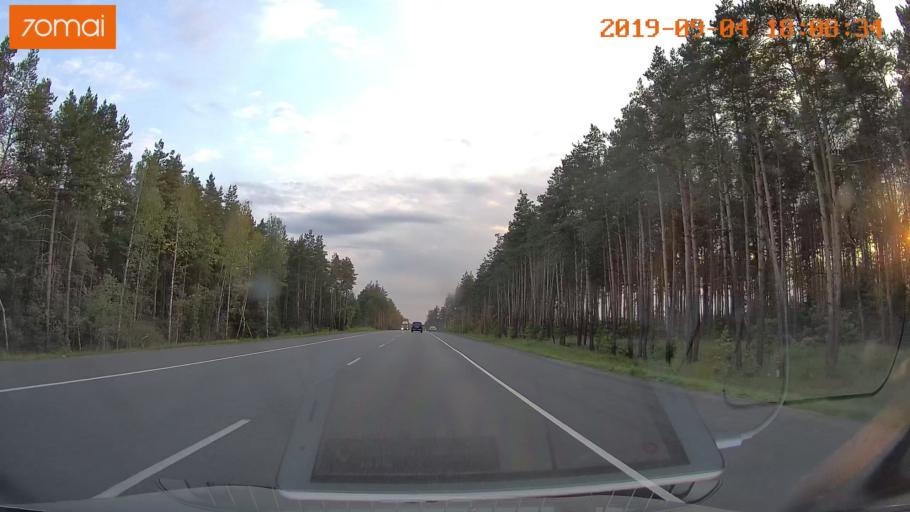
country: RU
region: Moskovskaya
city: Khorlovo
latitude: 55.4044
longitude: 38.7842
